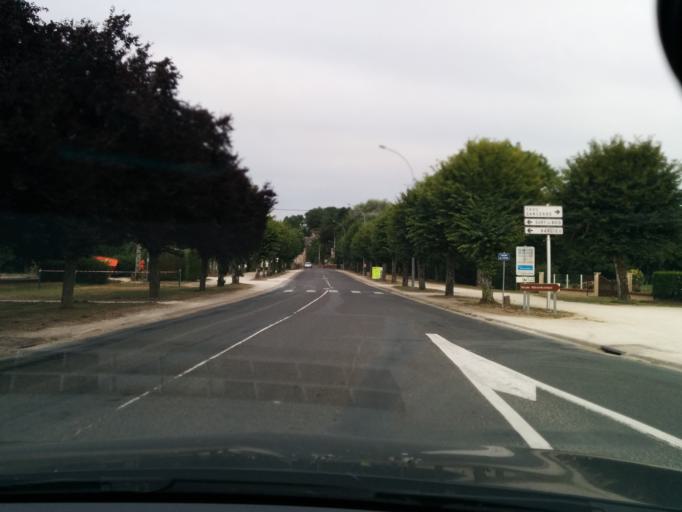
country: FR
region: Centre
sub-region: Departement du Cher
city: Blancafort
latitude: 47.4572
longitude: 2.6457
